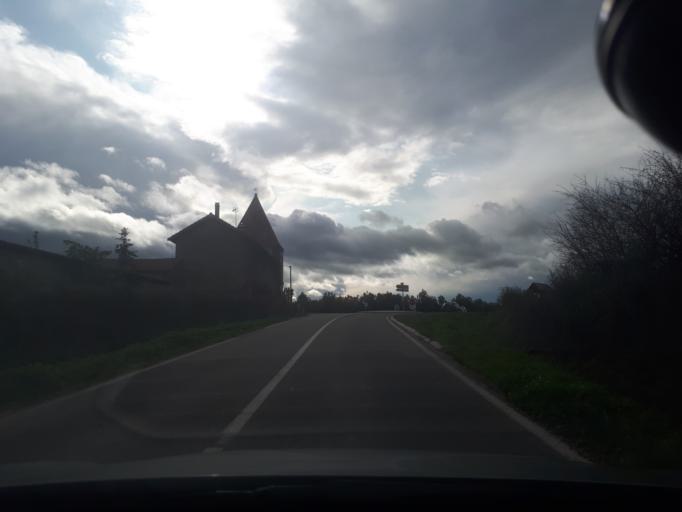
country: FR
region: Rhone-Alpes
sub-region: Departement de la Loire
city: Civens
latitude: 45.7328
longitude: 4.2884
